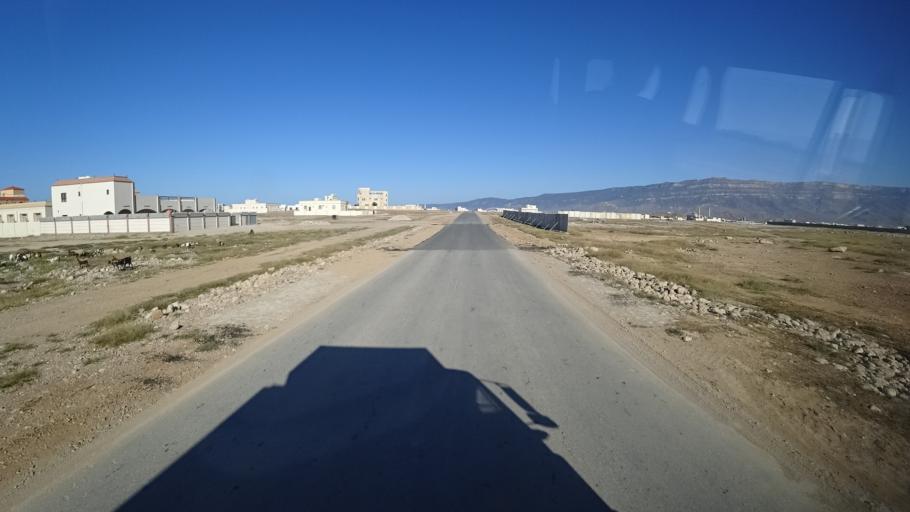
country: OM
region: Zufar
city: Salalah
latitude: 16.9786
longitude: 54.6998
